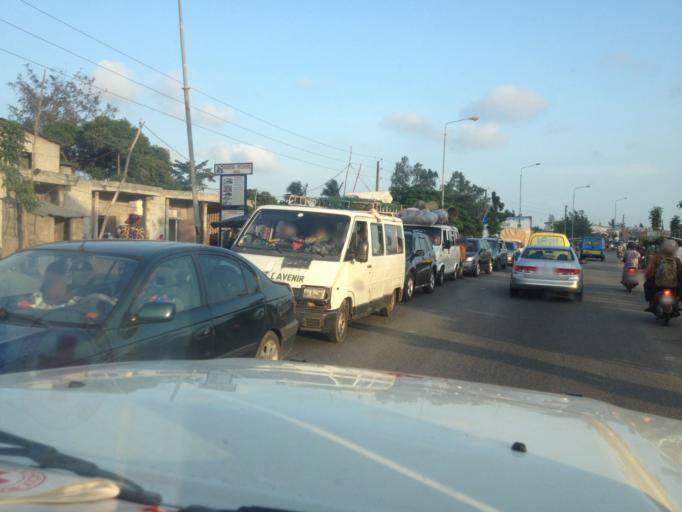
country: BJ
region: Queme
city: Porto-Novo
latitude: 6.4241
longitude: 2.6280
